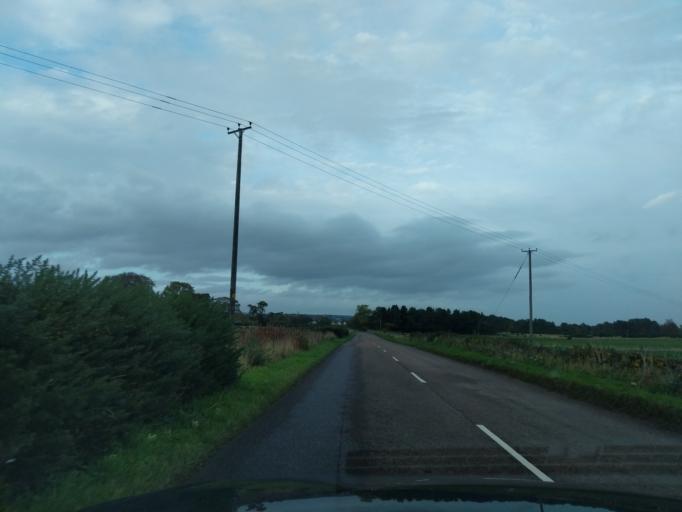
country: GB
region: Scotland
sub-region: Fife
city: Tayport
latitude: 56.4330
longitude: -2.8853
